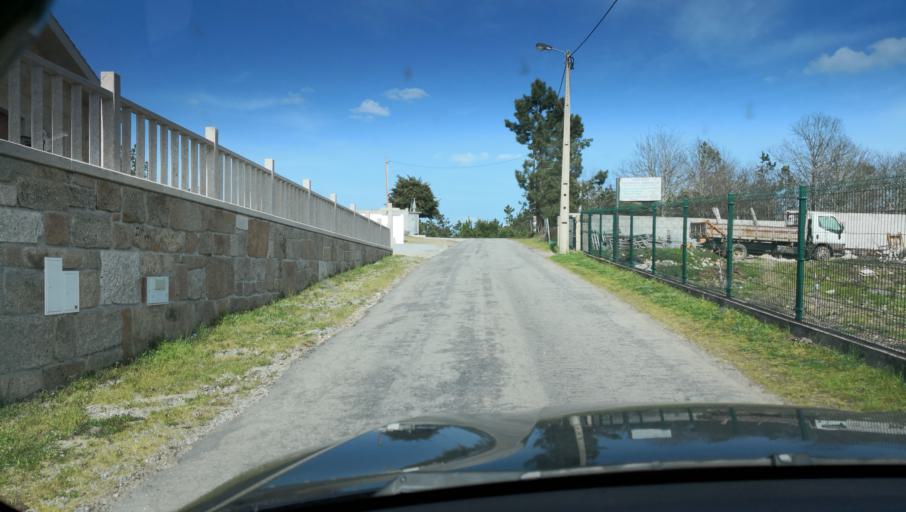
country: PT
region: Vila Real
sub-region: Sabrosa
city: Vilela
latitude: 41.2524
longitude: -7.6596
